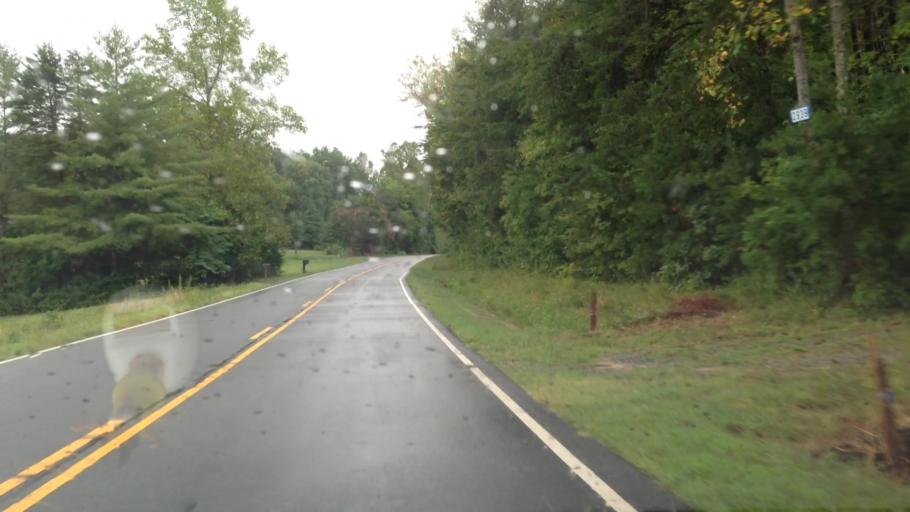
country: US
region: North Carolina
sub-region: Stokes County
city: Walnut Cove
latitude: 36.3799
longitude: -80.0926
